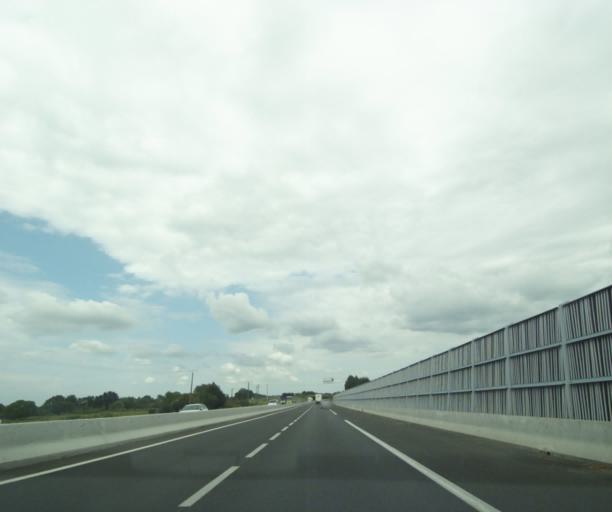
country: FR
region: Pays de la Loire
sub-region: Departement de Maine-et-Loire
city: Saumur
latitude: 47.2780
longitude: -0.0731
